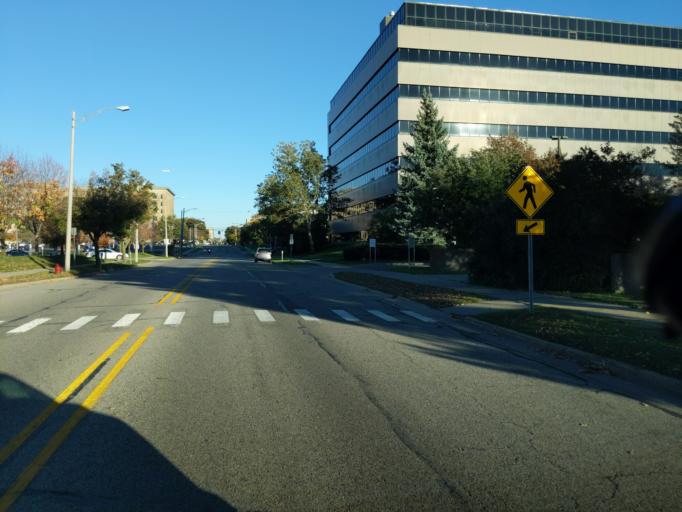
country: US
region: Michigan
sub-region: Ingham County
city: Lansing
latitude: 42.7300
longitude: -84.5619
